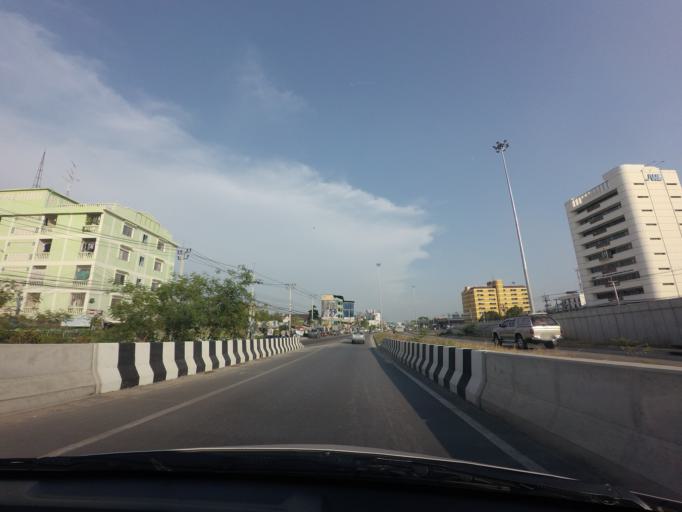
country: TH
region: Bangkok
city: Bang Kapi
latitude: 13.7512
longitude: 100.6473
